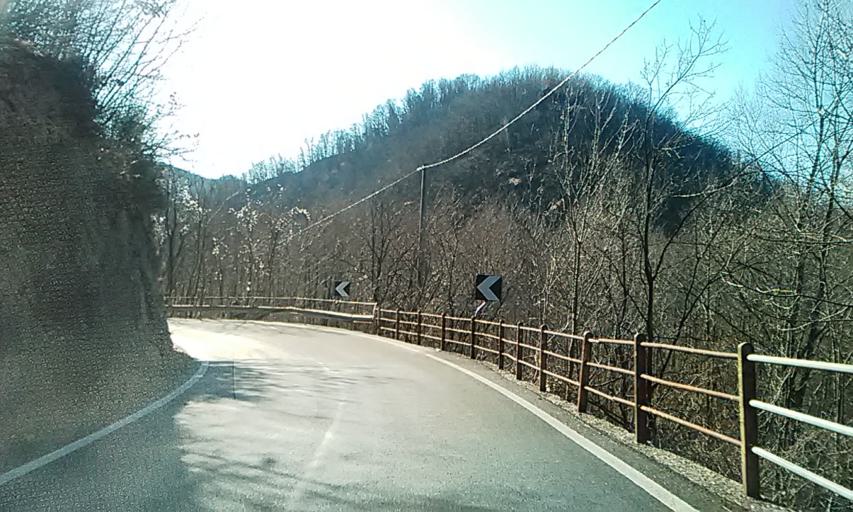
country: IT
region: Piedmont
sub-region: Provincia di Vercelli
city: Guardabosone
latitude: 45.6934
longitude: 8.2531
